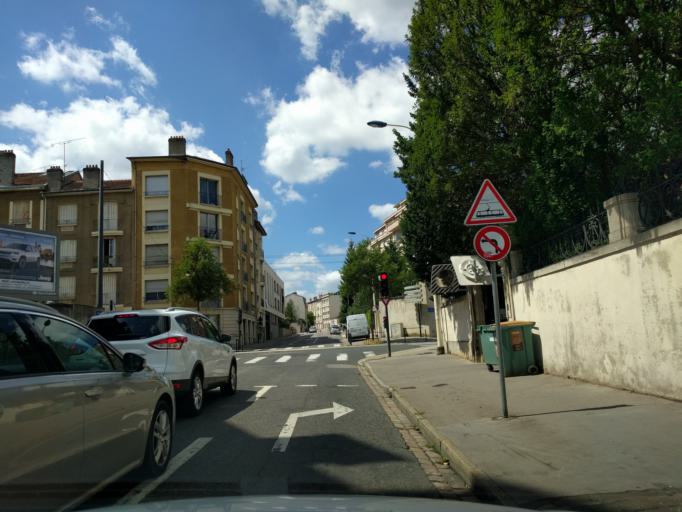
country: FR
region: Lorraine
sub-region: Departement de Meurthe-et-Moselle
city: Nancy
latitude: 48.6807
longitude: 6.1793
